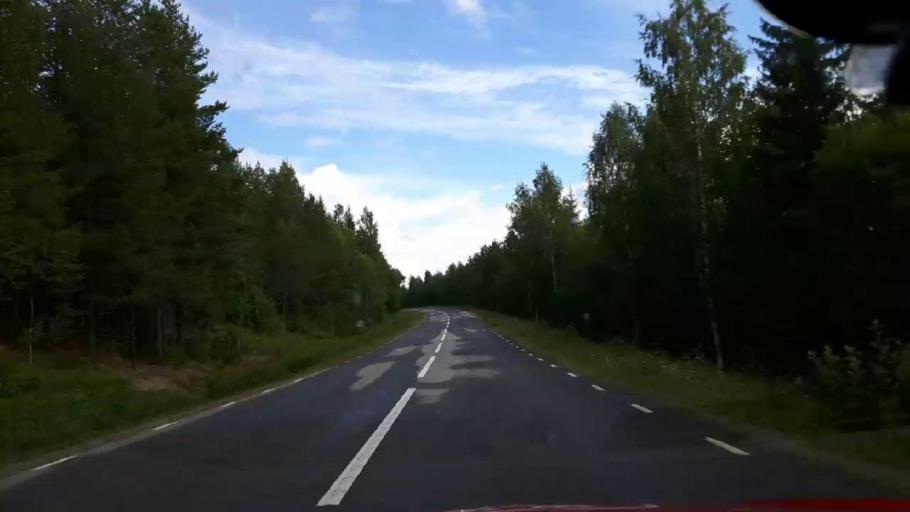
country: SE
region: Jaemtland
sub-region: Stroemsunds Kommun
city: Stroemsund
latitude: 64.3469
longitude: 15.0599
